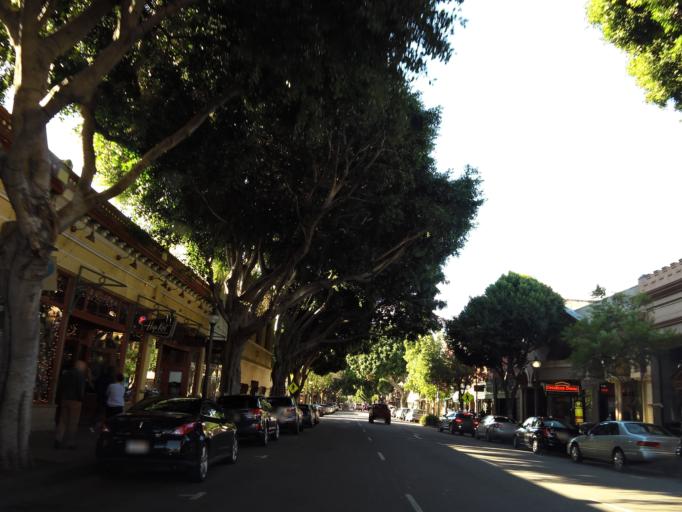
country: US
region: California
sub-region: San Luis Obispo County
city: San Luis Obispo
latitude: 35.2798
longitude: -120.6630
